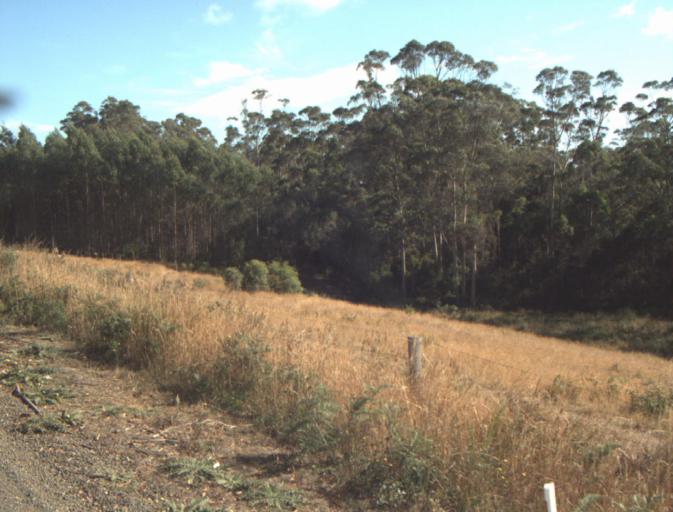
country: AU
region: Tasmania
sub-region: Dorset
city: Bridport
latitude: -41.1469
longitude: 147.2221
